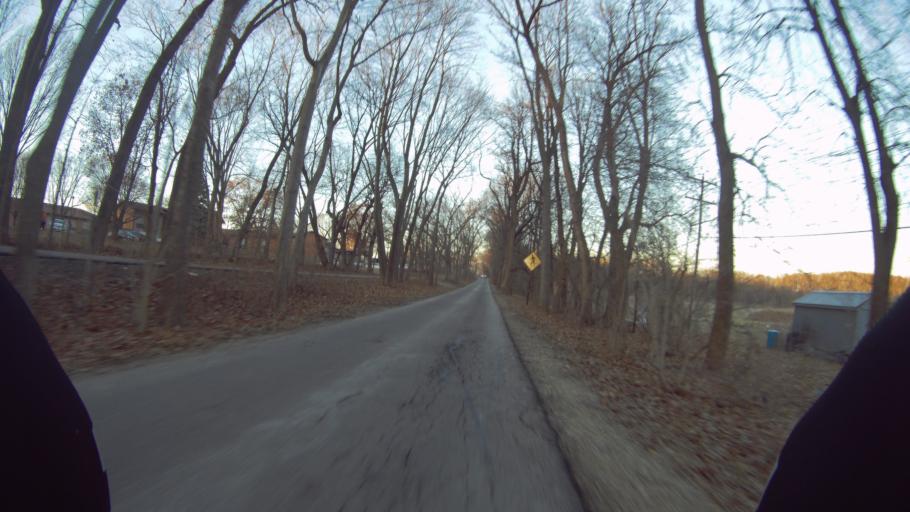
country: US
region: Wisconsin
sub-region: Dane County
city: Shorewood Hills
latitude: 43.0877
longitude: -89.4336
